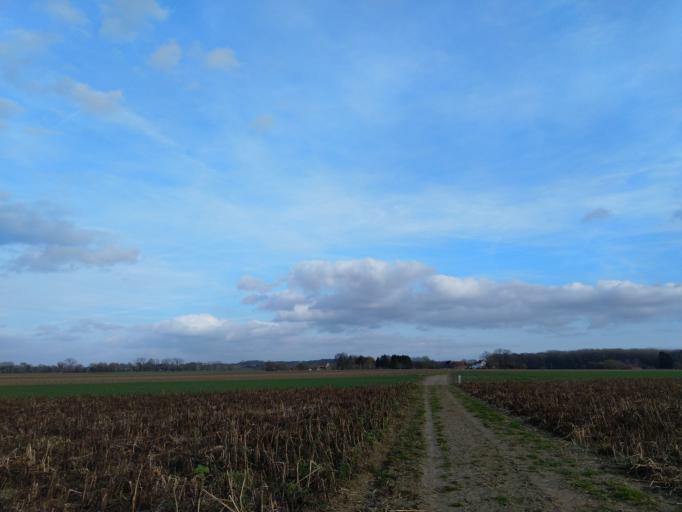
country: BE
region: Wallonia
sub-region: Province du Hainaut
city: Jurbise
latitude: 50.5241
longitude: 3.9293
